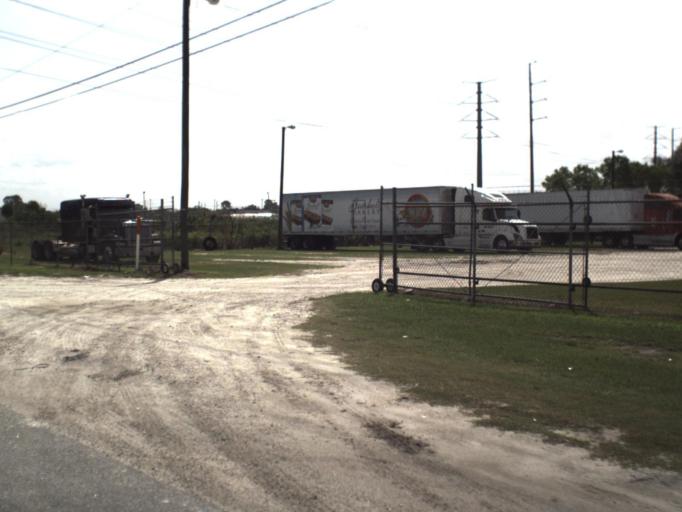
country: US
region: Florida
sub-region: Polk County
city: Auburndale
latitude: 28.0514
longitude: -81.8015
